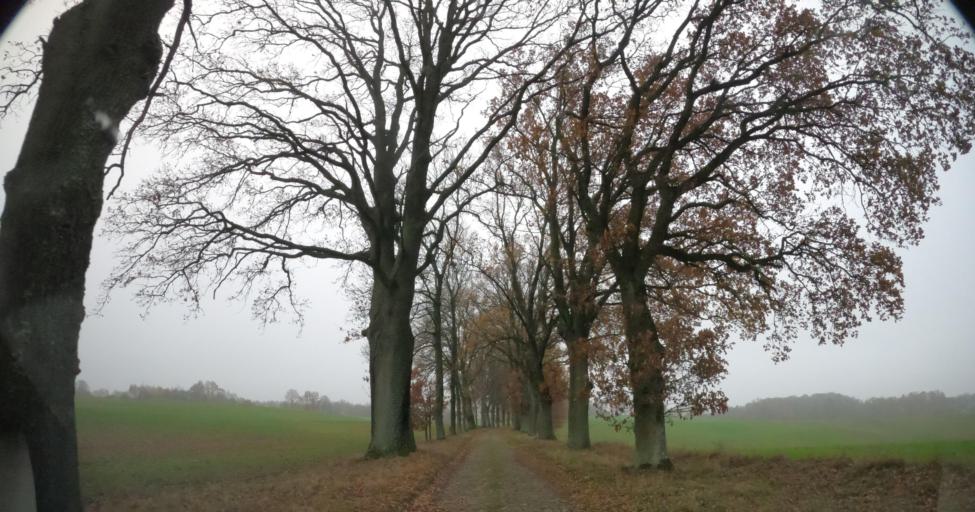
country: PL
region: West Pomeranian Voivodeship
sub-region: Powiat drawski
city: Drawsko Pomorskie
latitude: 53.5710
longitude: 15.7289
